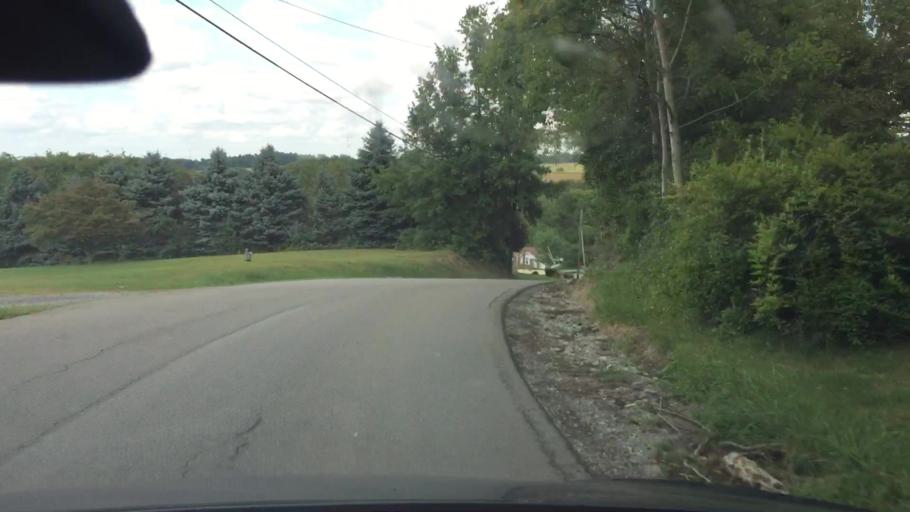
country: US
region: Pennsylvania
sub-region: Butler County
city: Meadowood
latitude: 40.8213
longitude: -79.8783
